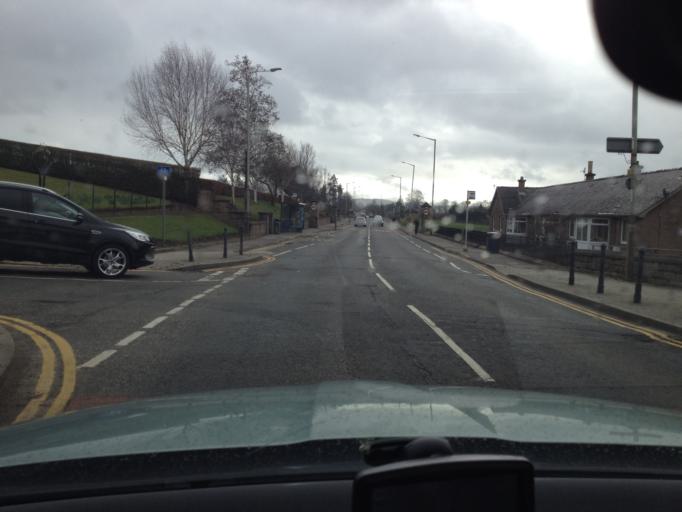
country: GB
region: Scotland
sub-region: Perth and Kinross
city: Scone
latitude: 56.4148
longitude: -3.4049
